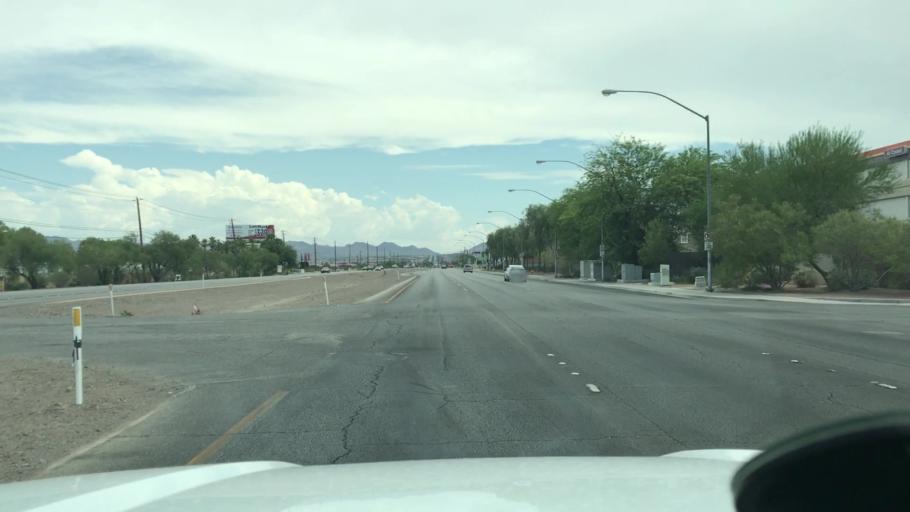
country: US
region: Nevada
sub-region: Clark County
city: Whitney
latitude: 36.0813
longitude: -115.0292
